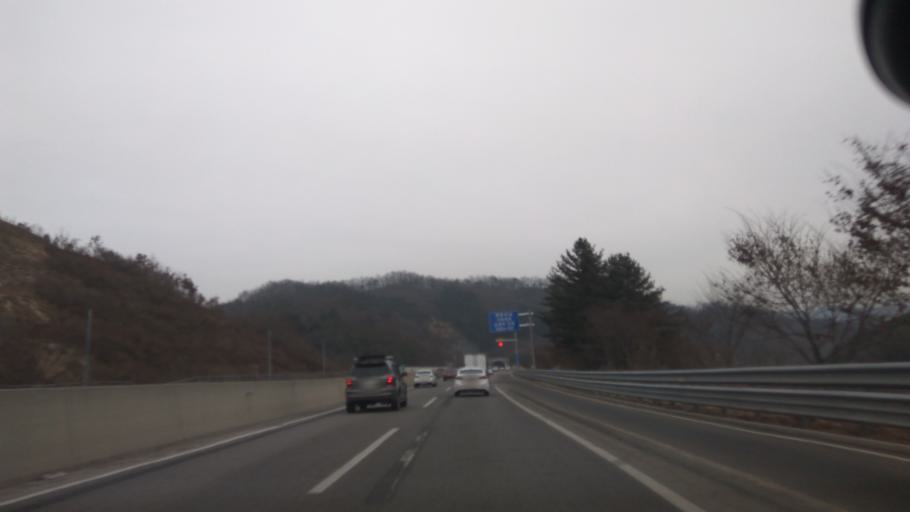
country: KR
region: Gangwon-do
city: Sindong
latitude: 37.7422
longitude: 127.6760
